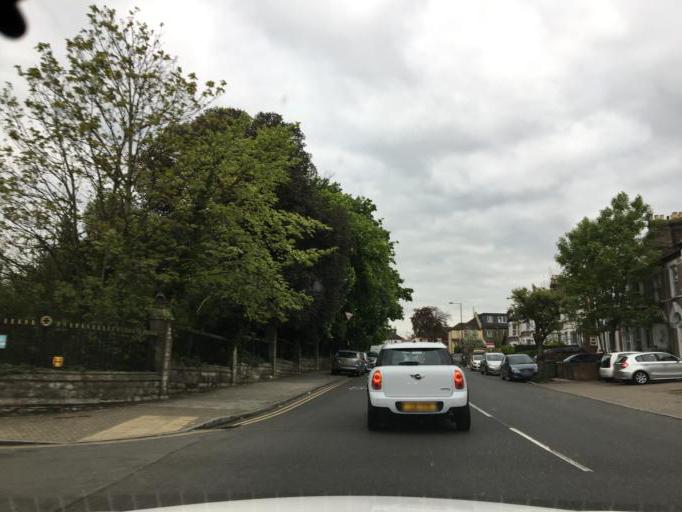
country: GB
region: England
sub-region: Greater London
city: Blackheath
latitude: 51.4387
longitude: 0.0056
